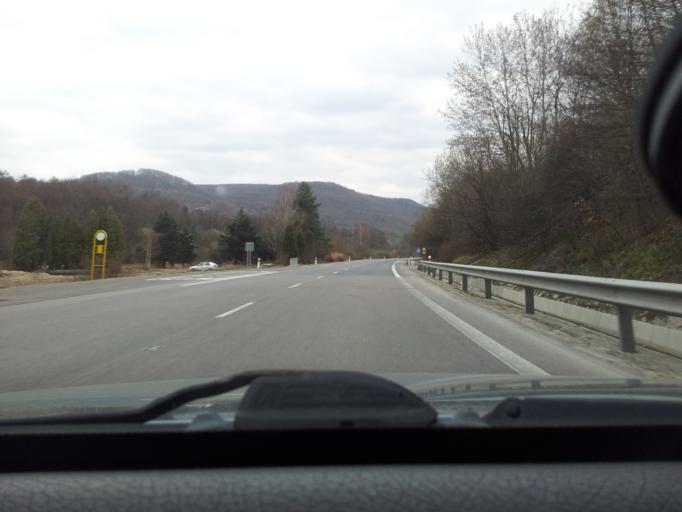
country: SK
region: Banskobystricky
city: Ziar nad Hronom
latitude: 48.6342
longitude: 18.9020
